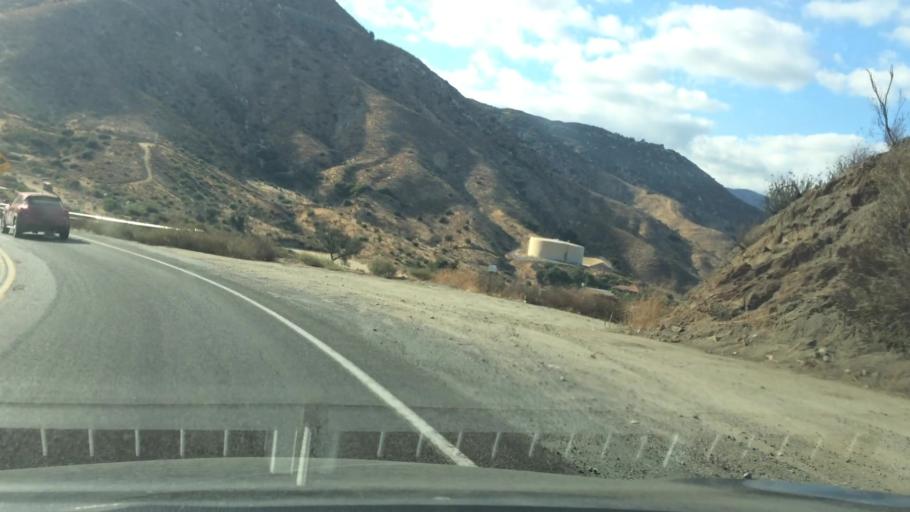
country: US
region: California
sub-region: Riverside County
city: Lakeland Village
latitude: 33.6491
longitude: -117.3743
